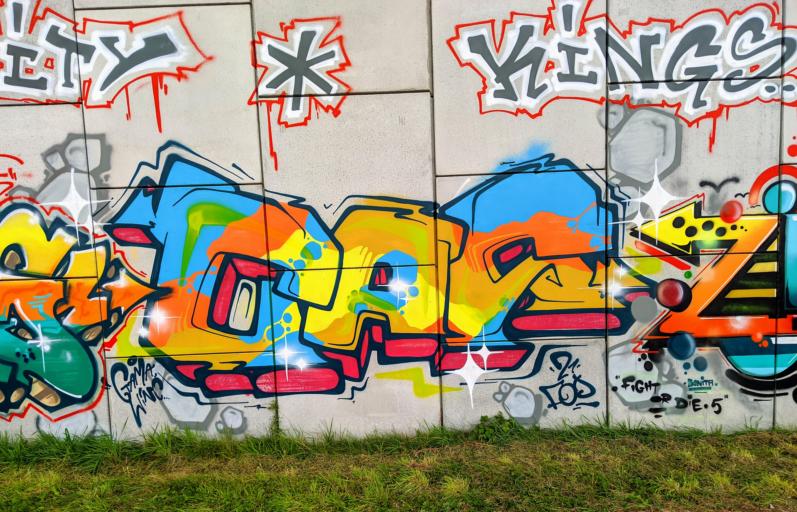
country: PL
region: Lubusz
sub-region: Powiat nowosolski
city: Nowa Sol
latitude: 51.7877
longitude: 15.7148
